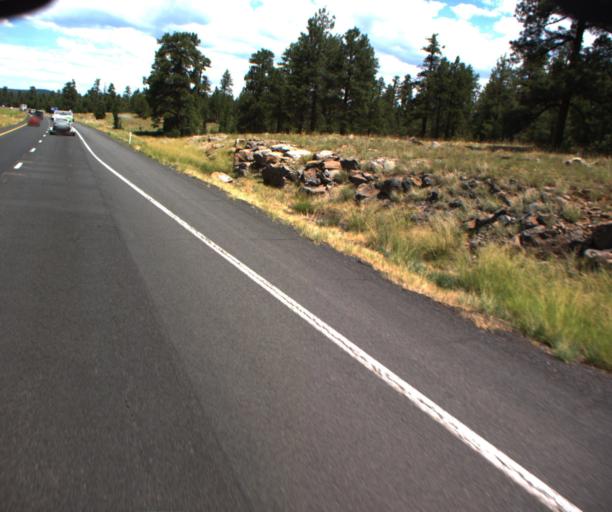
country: US
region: Arizona
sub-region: Coconino County
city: Sedona
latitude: 34.9165
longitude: -111.6417
